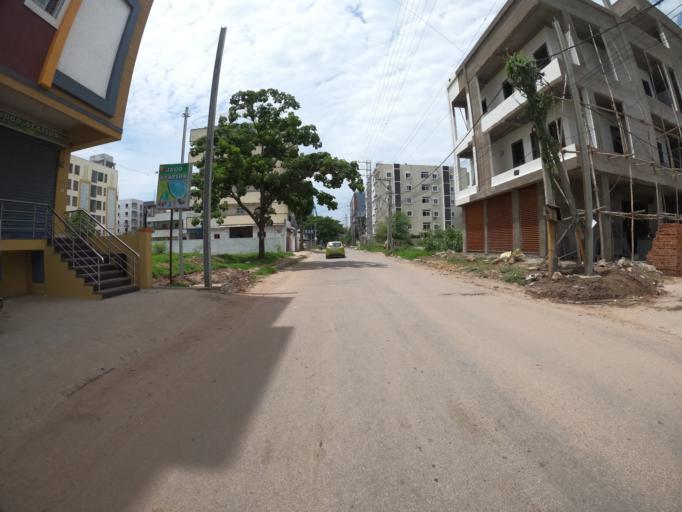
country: IN
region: Telangana
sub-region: Hyderabad
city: Hyderabad
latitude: 17.3700
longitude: 78.4126
